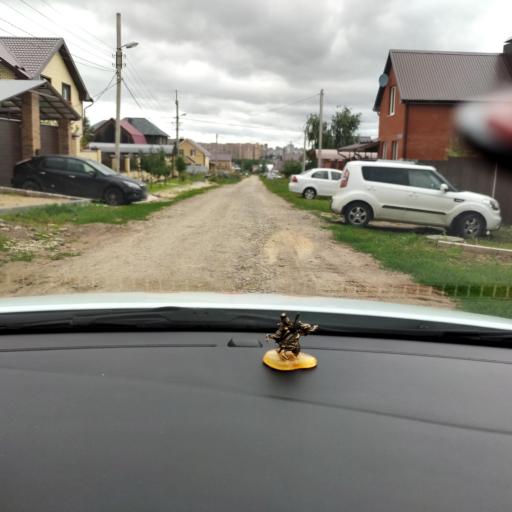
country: RU
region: Tatarstan
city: Vysokaya Gora
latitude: 55.7807
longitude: 49.2707
